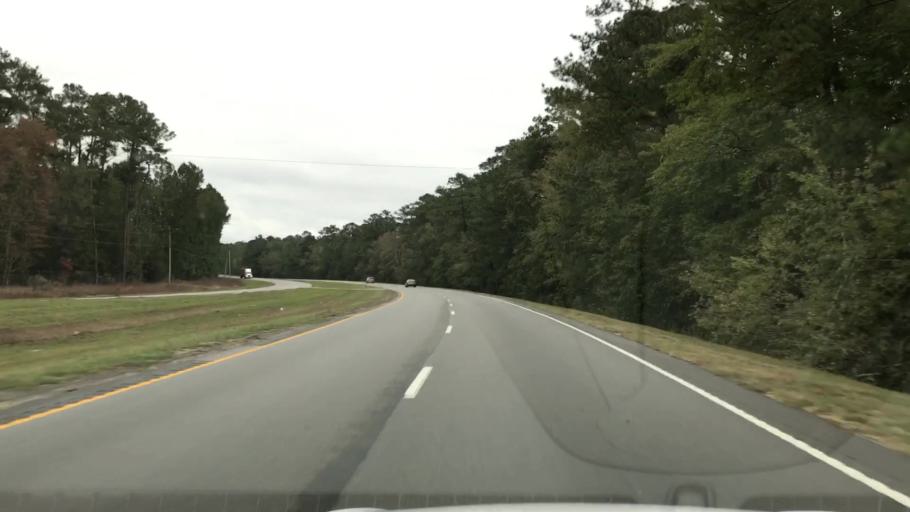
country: US
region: South Carolina
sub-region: Georgetown County
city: Georgetown
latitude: 33.2738
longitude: -79.3534
